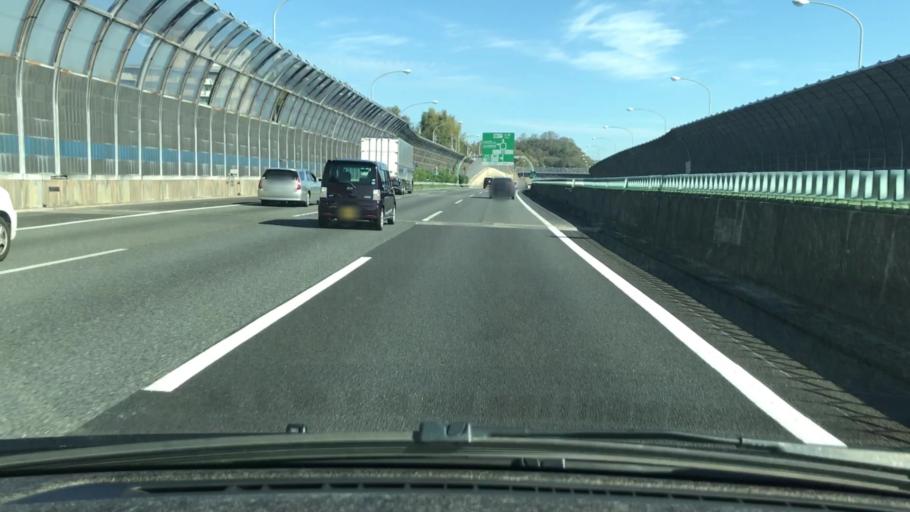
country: JP
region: Osaka
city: Takatsuki
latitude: 34.8505
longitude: 135.5819
